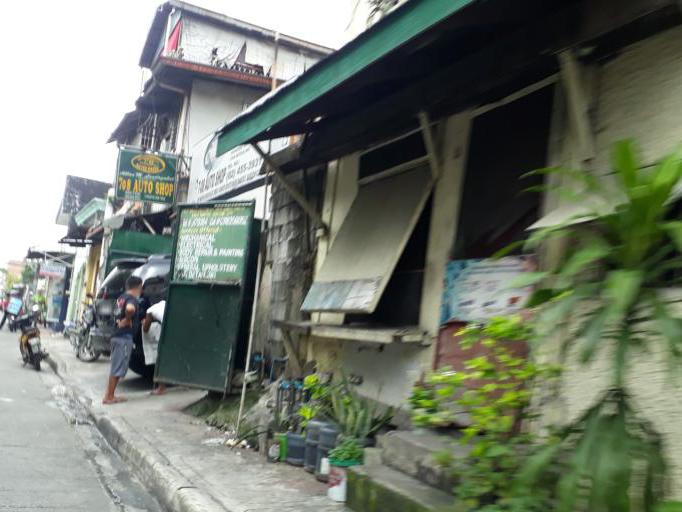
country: PH
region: Calabarzon
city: Bagong Pagasa
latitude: 14.6600
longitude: 121.0307
